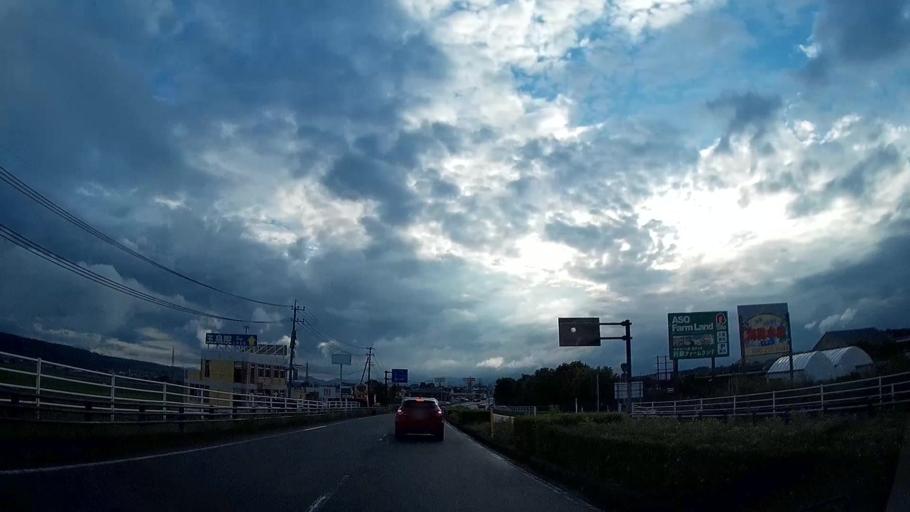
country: JP
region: Kumamoto
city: Ozu
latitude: 32.8758
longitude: 130.8813
